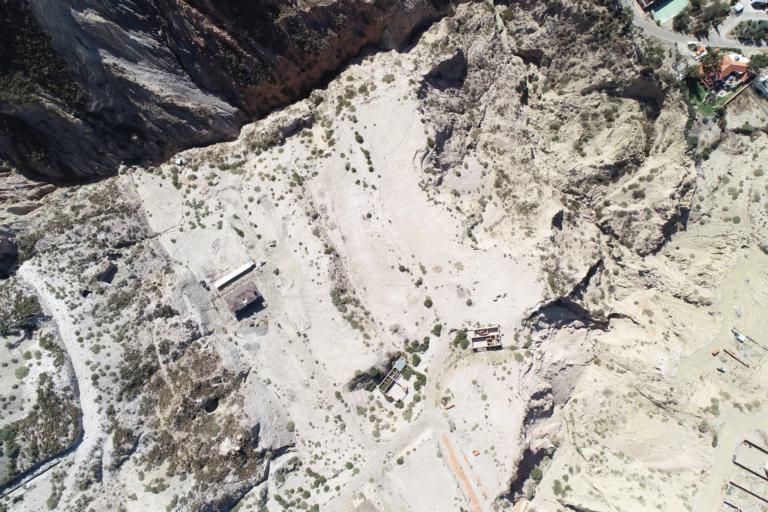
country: BO
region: La Paz
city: La Paz
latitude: -16.5560
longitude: -68.1062
